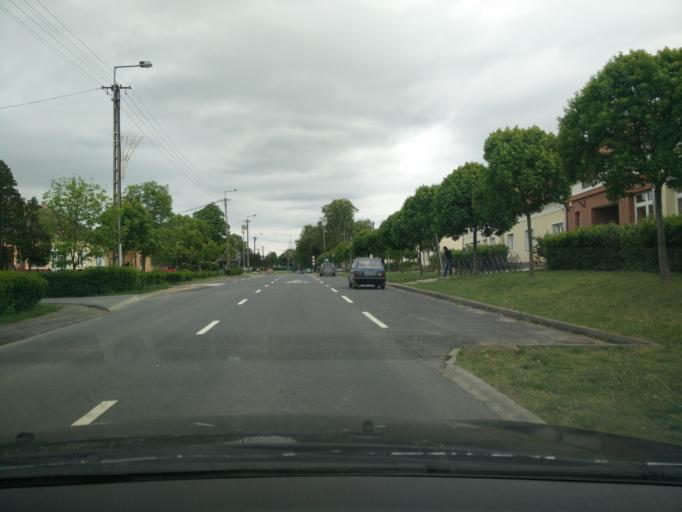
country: HU
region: Zala
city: Turje
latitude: 46.9839
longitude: 17.1048
